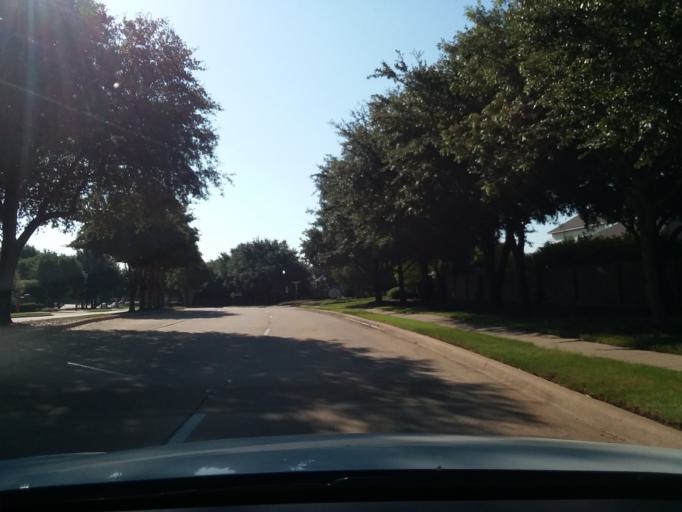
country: US
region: Texas
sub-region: Denton County
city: Flower Mound
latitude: 33.0272
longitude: -97.0937
